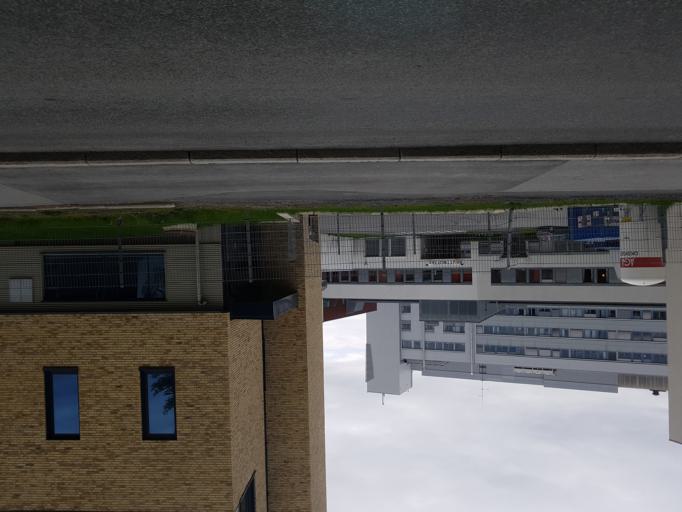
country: NO
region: Nord-Trondelag
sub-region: Levanger
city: Levanger
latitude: 63.7422
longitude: 11.2869
